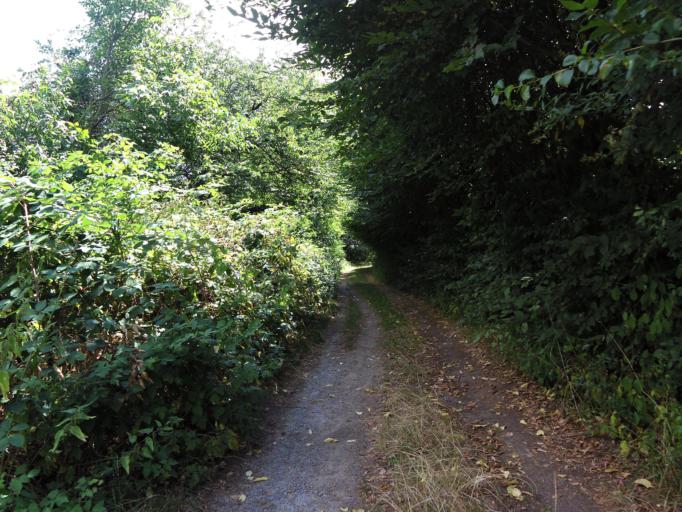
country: DE
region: Bavaria
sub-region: Regierungsbezirk Unterfranken
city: Randersacker
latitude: 49.7618
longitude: 9.9672
